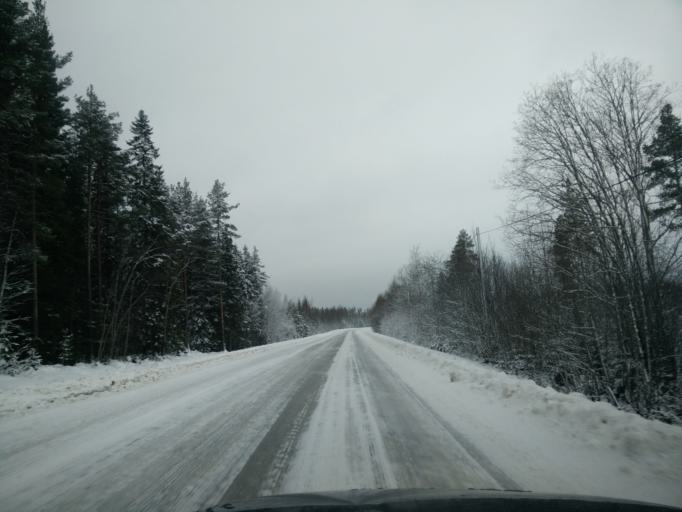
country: SE
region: Vaesternorrland
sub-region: Ange Kommun
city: Ange
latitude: 62.4004
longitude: 15.3271
